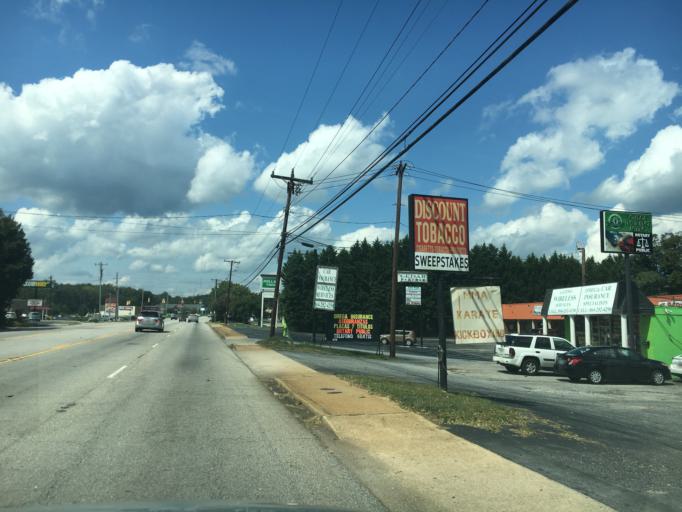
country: US
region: South Carolina
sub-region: Greenville County
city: Berea
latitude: 34.8825
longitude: -82.4529
